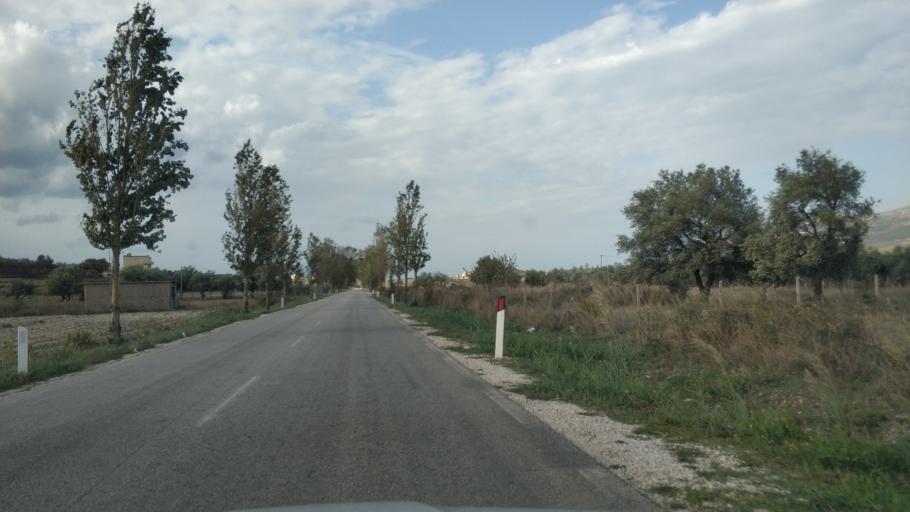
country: AL
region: Vlore
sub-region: Rrethi i Vlores
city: Orikum
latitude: 40.3185
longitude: 19.4833
